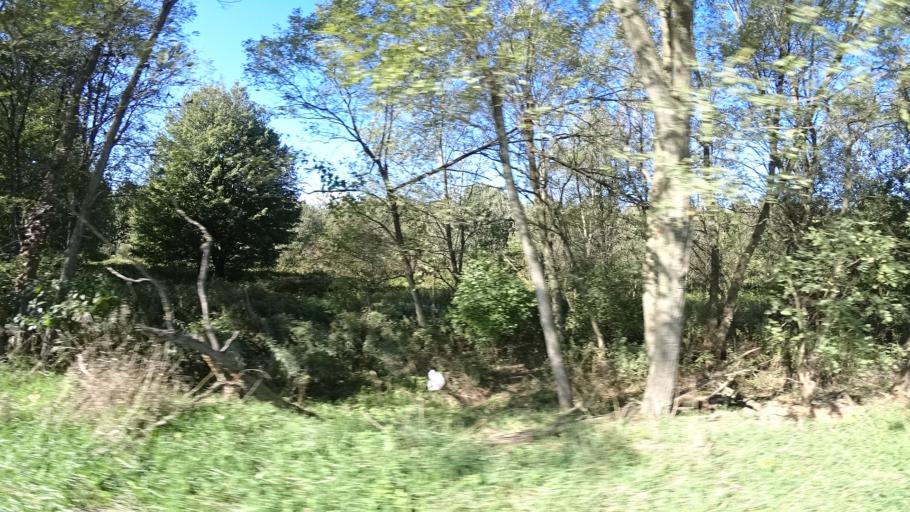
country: US
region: Indiana
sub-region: LaPorte County
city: Michigan City
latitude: 41.6866
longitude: -86.9132
